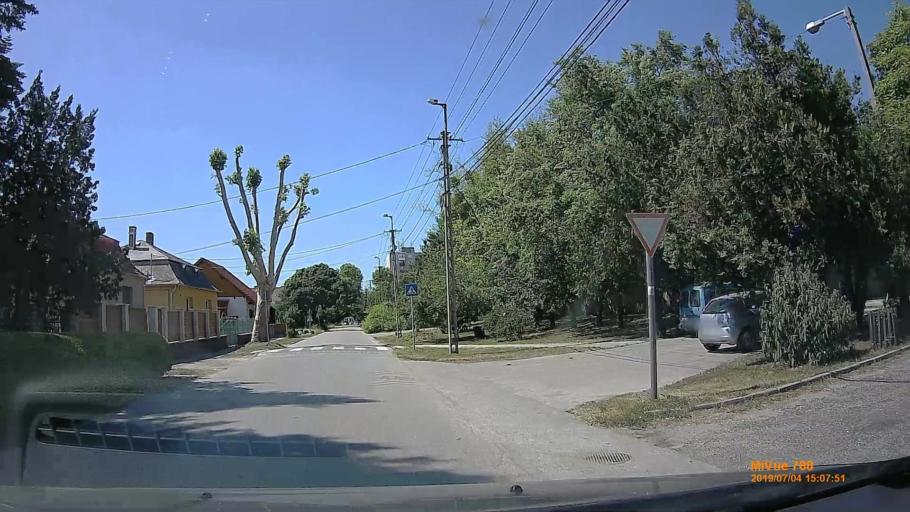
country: HU
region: Komarom-Esztergom
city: Tatabanya
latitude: 47.5751
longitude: 18.3908
